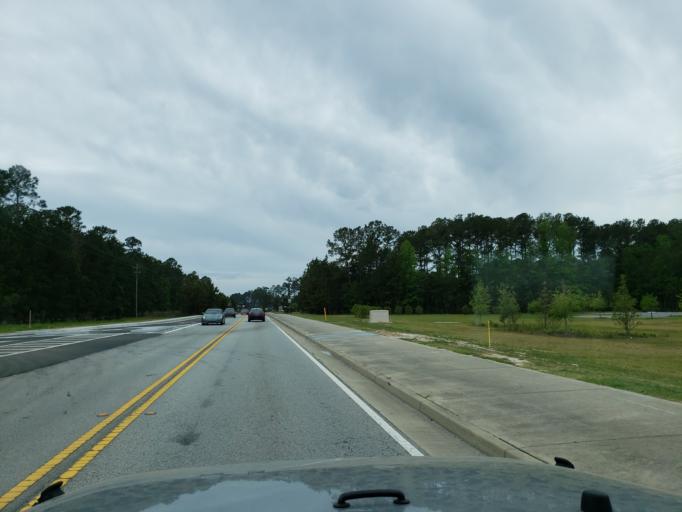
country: US
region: Georgia
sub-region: Chatham County
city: Pooler
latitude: 32.1560
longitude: -81.2386
